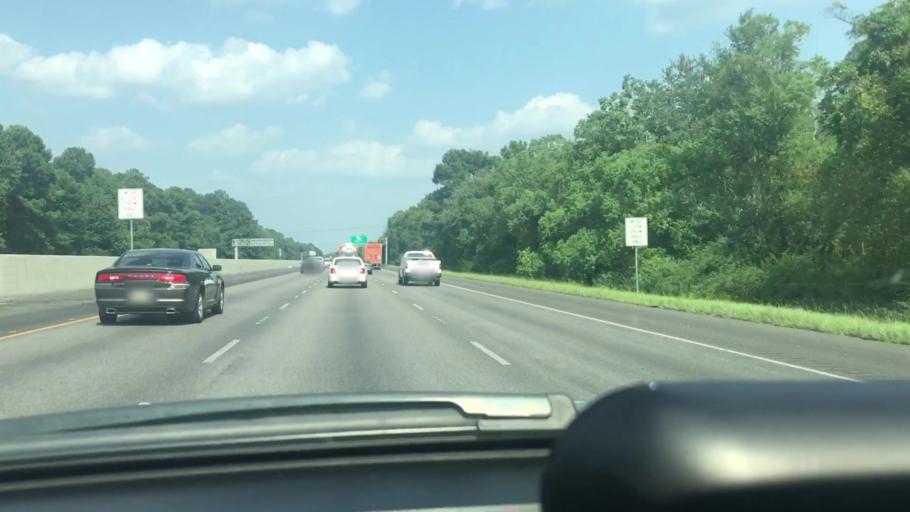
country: US
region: Louisiana
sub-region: Livingston Parish
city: Walker
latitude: 30.4657
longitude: -90.9031
